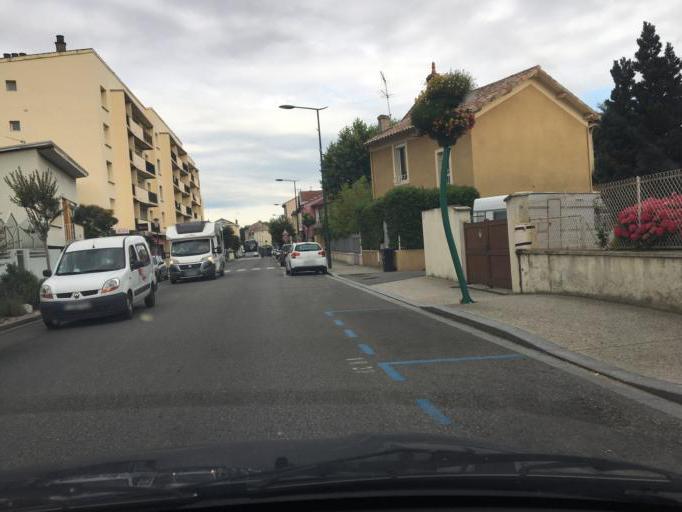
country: FR
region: Rhone-Alpes
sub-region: Departement de l'Ardeche
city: Guilherand-Granges
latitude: 44.9342
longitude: 4.8776
